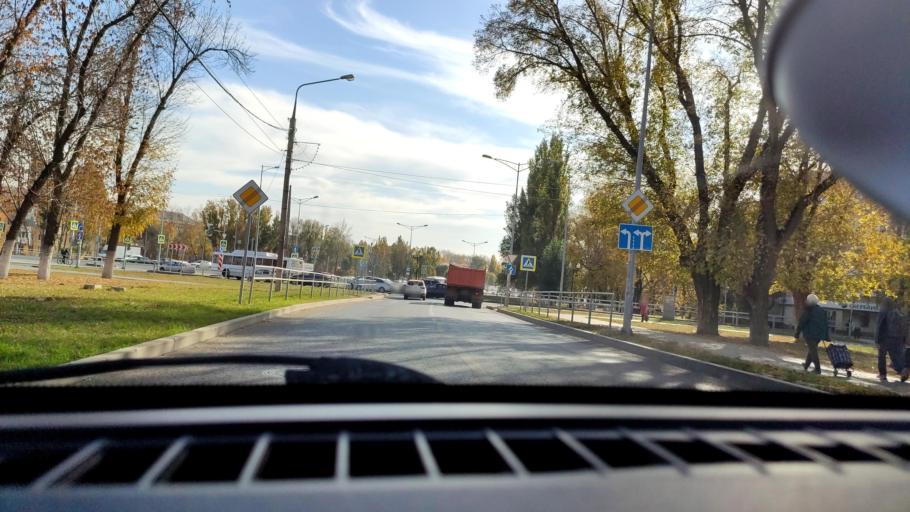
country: RU
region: Samara
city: Petra-Dubrava
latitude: 53.2989
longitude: 50.2862
